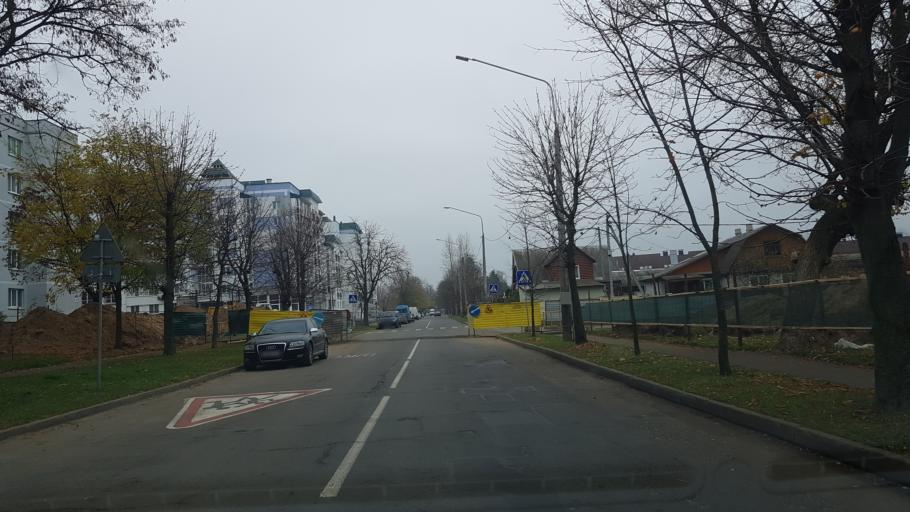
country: BY
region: Mogilev
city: Babruysk
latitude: 53.1512
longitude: 29.2418
